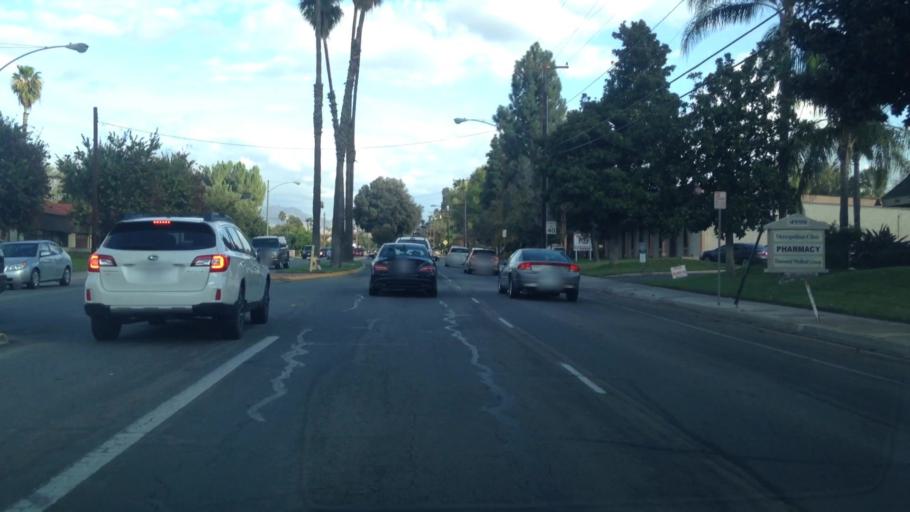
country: US
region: California
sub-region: Riverside County
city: Riverside
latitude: 33.9461
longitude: -117.4123
